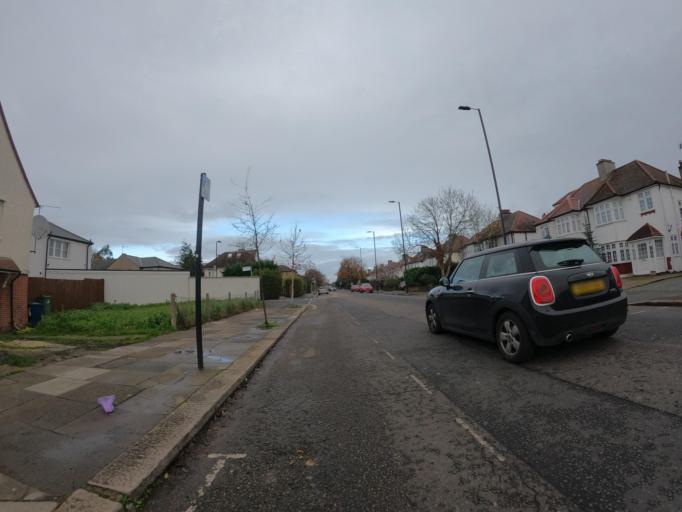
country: GB
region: England
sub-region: Greater London
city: Ealing
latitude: 51.5004
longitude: -0.2976
